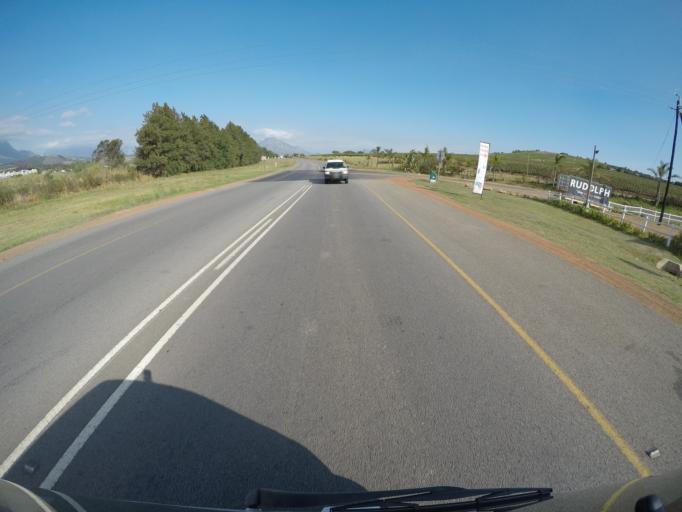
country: ZA
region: Western Cape
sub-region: Cape Winelands District Municipality
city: Stellenbosch
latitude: -33.8778
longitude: 18.8148
